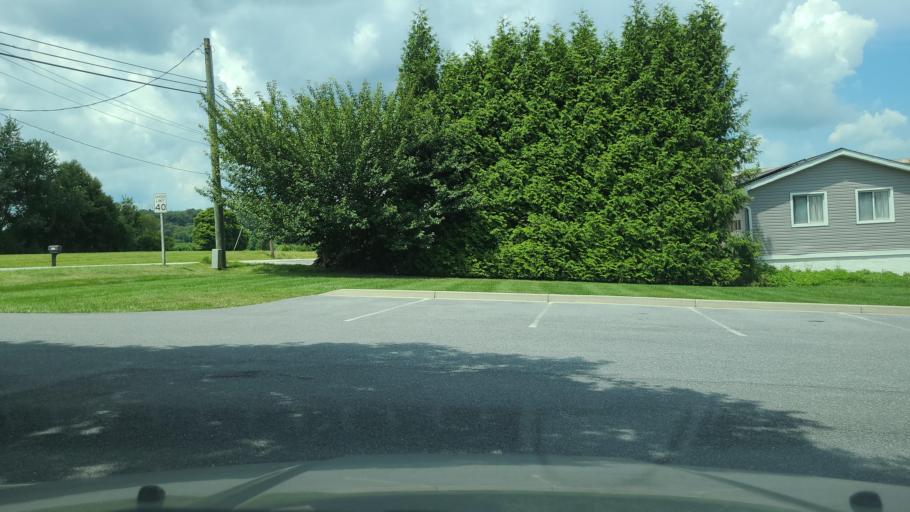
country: US
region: Maryland
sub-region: Carroll County
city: Eldersburg
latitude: 39.4417
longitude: -77.0397
